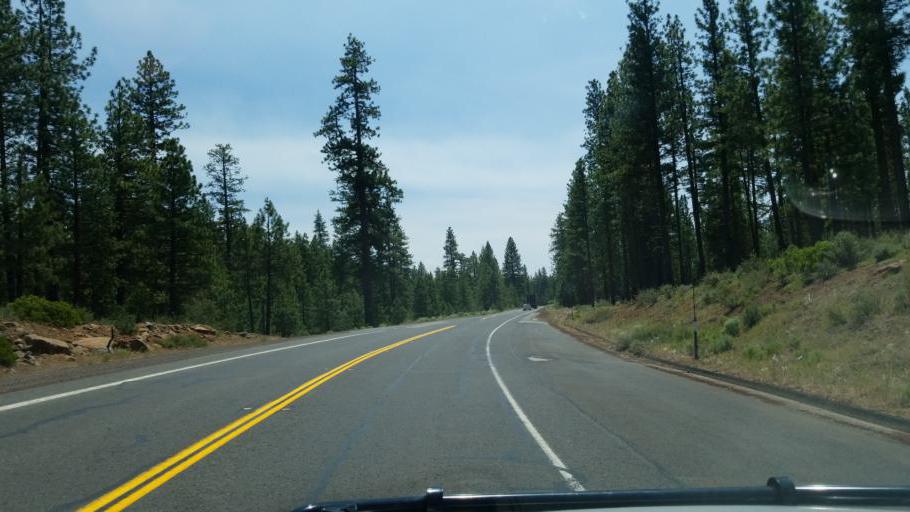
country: US
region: California
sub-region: Shasta County
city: Burney
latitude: 40.6946
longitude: -121.3853
